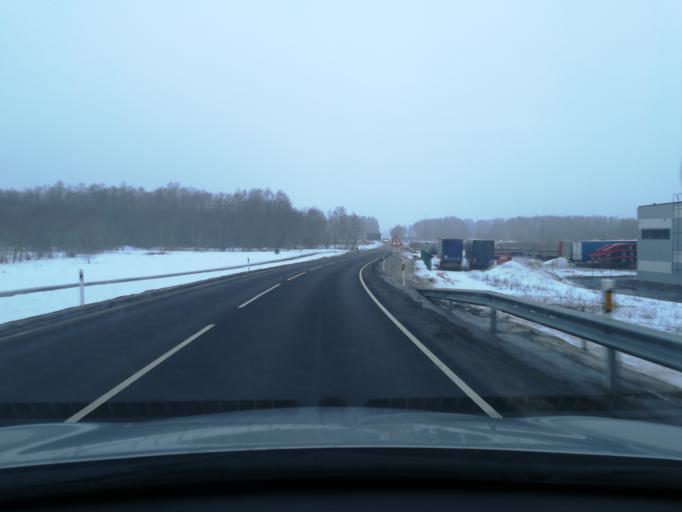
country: EE
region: Harju
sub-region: Rae vald
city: Jueri
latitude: 59.3732
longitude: 24.9061
